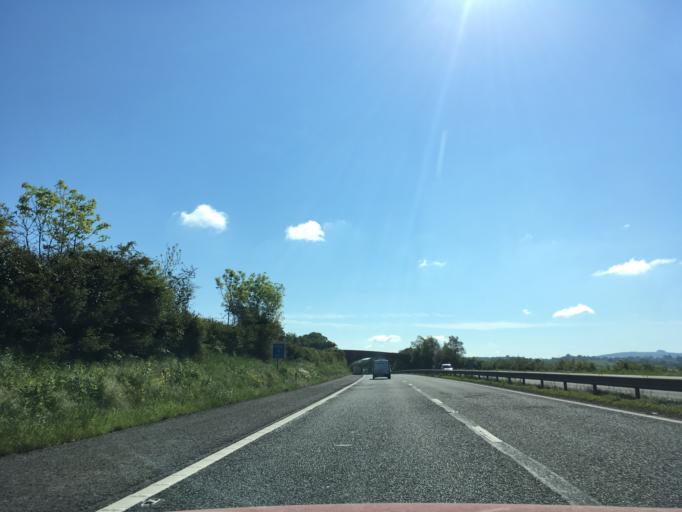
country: GB
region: England
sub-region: Herefordshire
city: Ross on Wye
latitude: 51.9291
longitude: -2.5539
